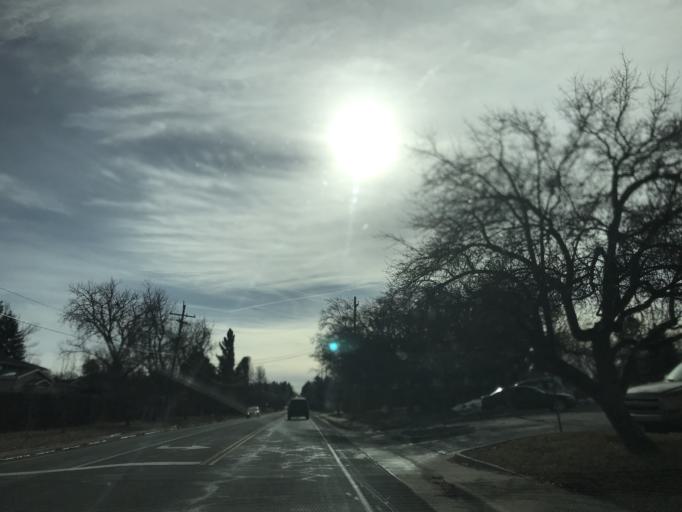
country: US
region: Colorado
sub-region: Arapahoe County
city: Columbine Valley
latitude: 39.5946
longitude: -105.0164
